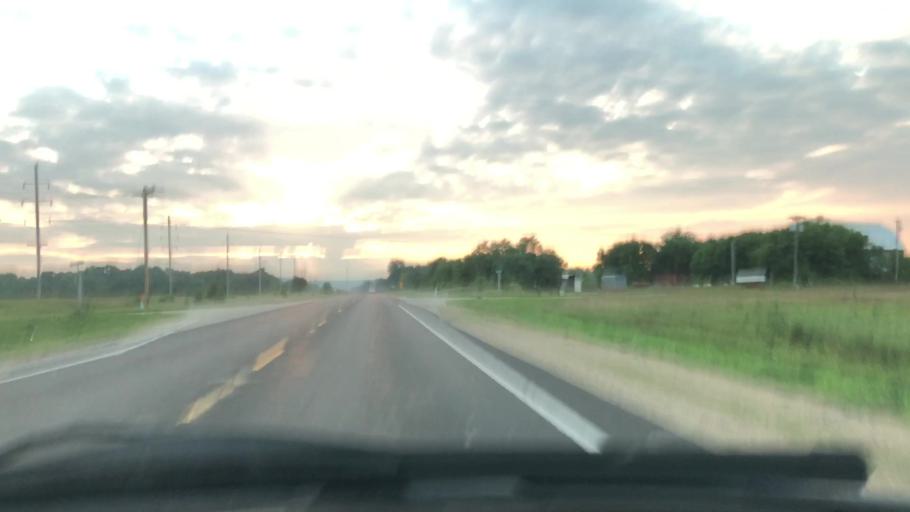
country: US
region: Wisconsin
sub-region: Sauk County
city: Spring Green
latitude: 43.2036
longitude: -90.2511
